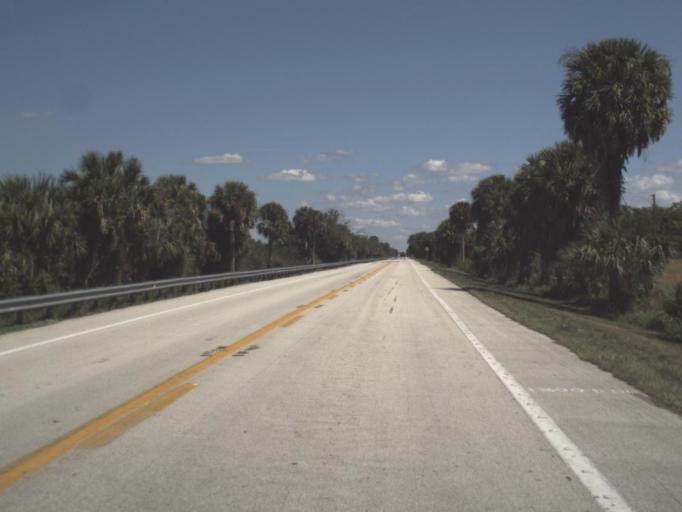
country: US
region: Florida
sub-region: Glades County
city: Buckhead Ridge
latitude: 27.1081
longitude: -80.9427
